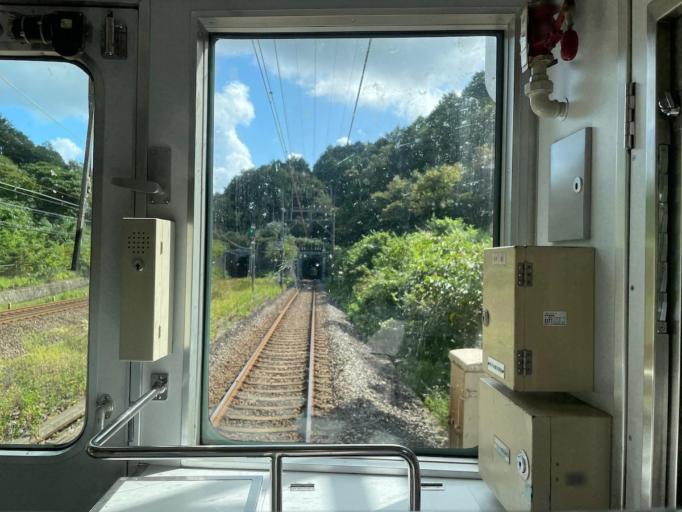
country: JP
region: Mie
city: Toba
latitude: 34.4751
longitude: 136.8004
